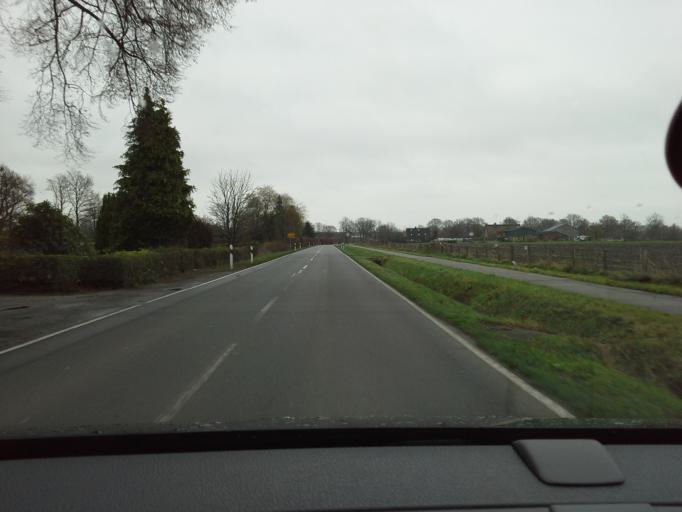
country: DE
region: Schleswig-Holstein
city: Hemdingen
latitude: 53.7655
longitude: 9.8483
